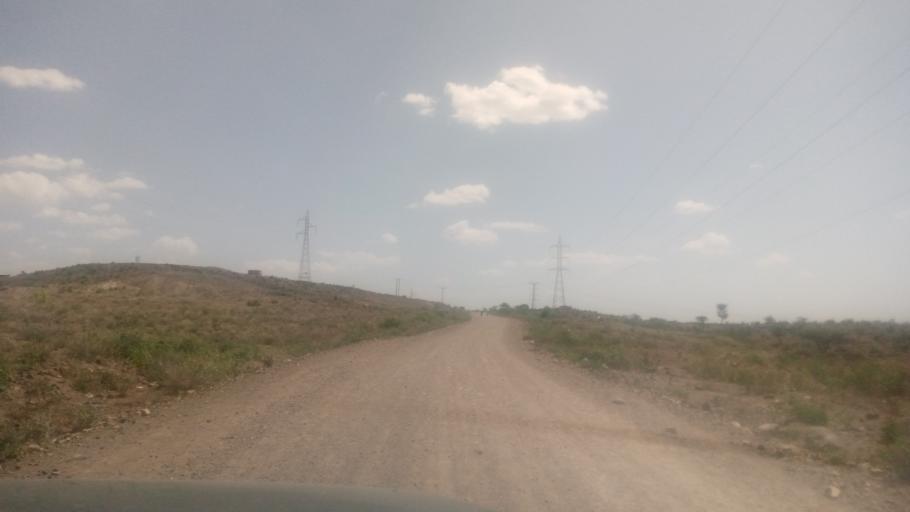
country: ET
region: Oromiya
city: Deder
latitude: 9.5268
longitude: 41.3439
